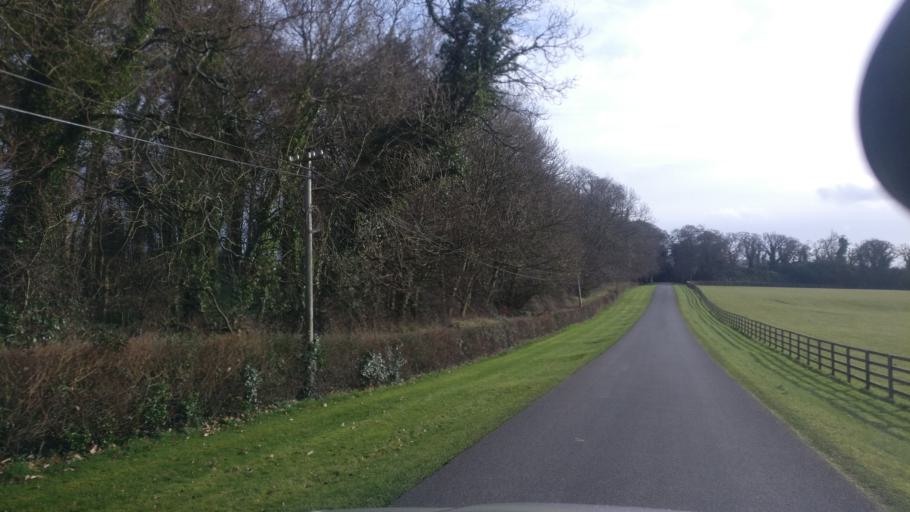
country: IE
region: Leinster
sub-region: Kilkenny
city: Thomastown
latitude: 52.5307
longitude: -7.1720
